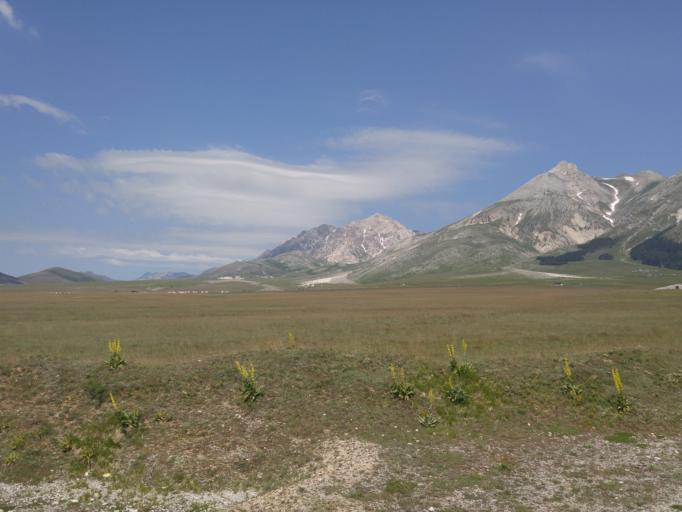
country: IT
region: Abruzzo
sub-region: Provincia dell' Aquila
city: Castel del Monte
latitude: 42.4047
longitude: 13.7592
